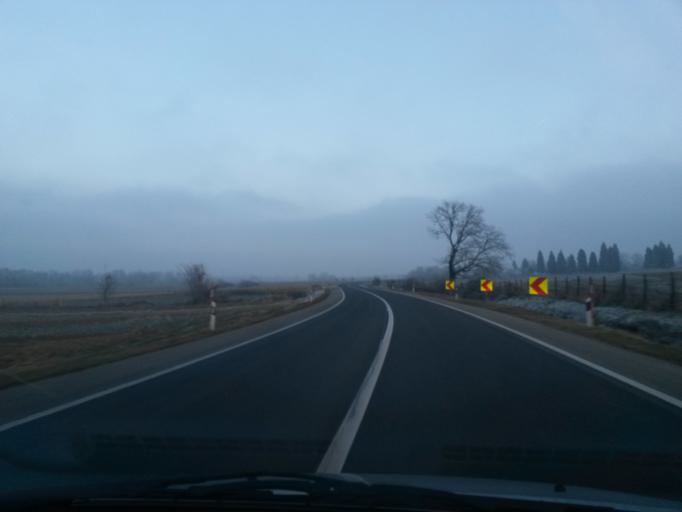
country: HR
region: Varazdinska
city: Ludbreg
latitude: 46.2147
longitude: 16.6897
